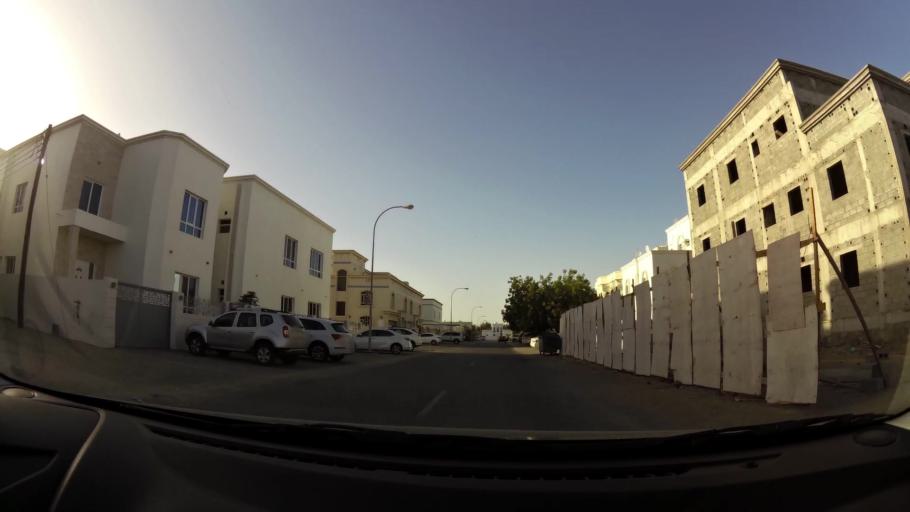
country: OM
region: Muhafazat Masqat
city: As Sib al Jadidah
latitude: 23.6109
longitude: 58.2292
